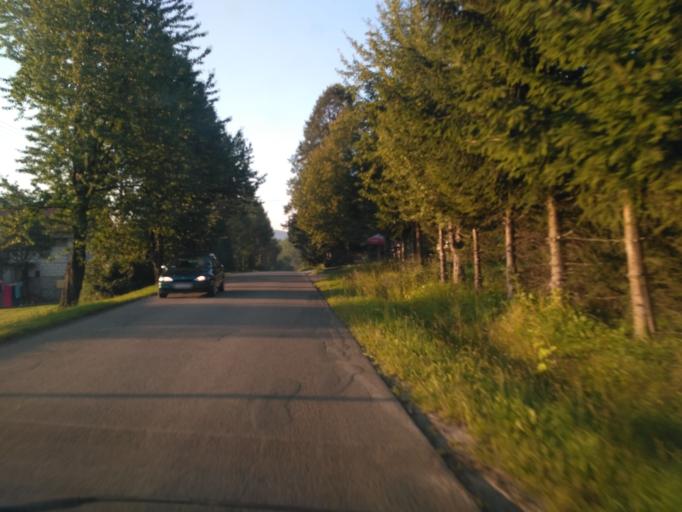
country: PL
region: Subcarpathian Voivodeship
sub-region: Powiat strzyzowski
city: Wysoka Strzyzowska
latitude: 49.8096
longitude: 21.7448
